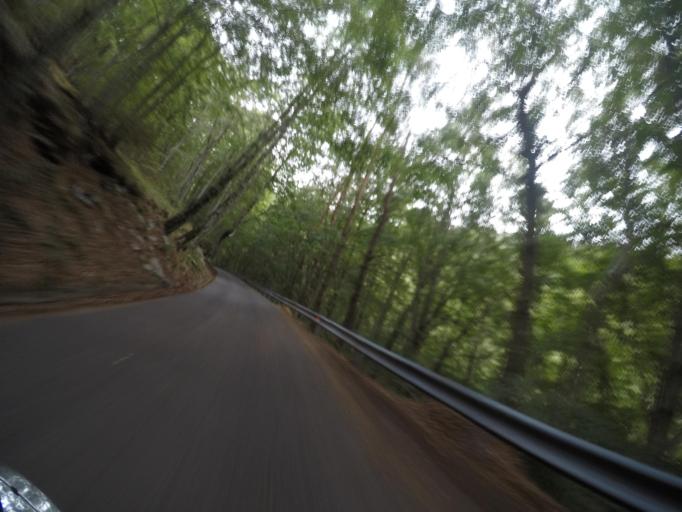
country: IT
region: Tuscany
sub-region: Provincia di Massa-Carrara
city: Carrara
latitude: 44.1168
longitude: 10.1200
